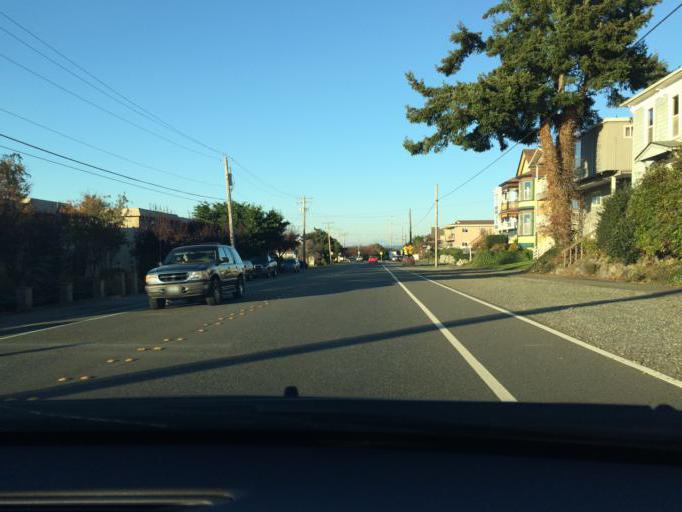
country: US
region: Washington
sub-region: Whatcom County
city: Bellingham
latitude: 48.7265
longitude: -122.5038
